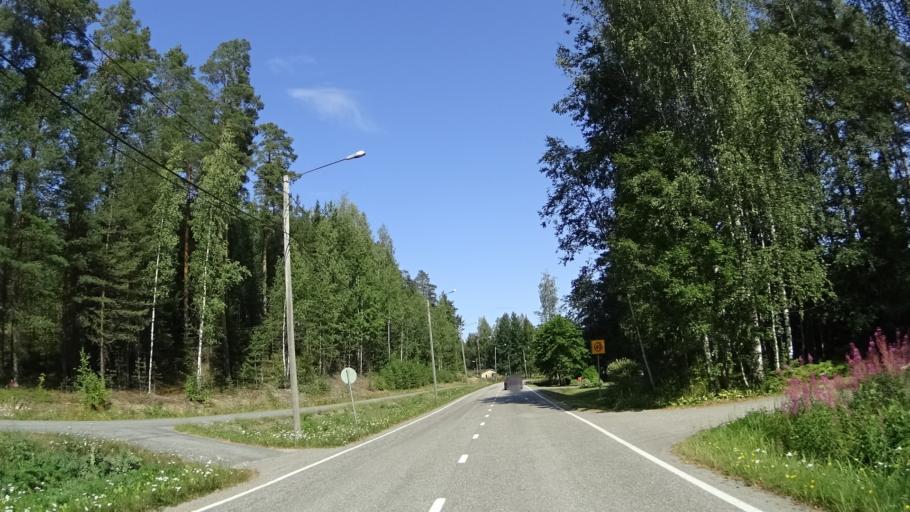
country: FI
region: Pirkanmaa
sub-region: Ylae-Pirkanmaa
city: Maenttae
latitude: 61.8583
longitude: 24.8234
